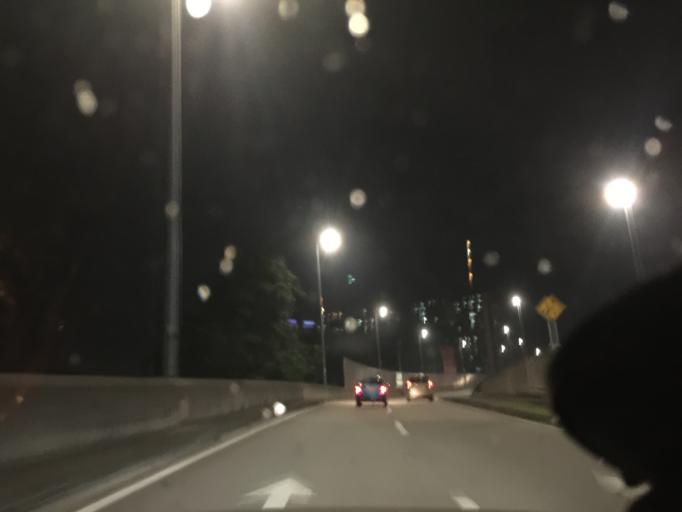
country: MY
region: Kuala Lumpur
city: Kuala Lumpur
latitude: 3.1596
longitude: 101.7035
